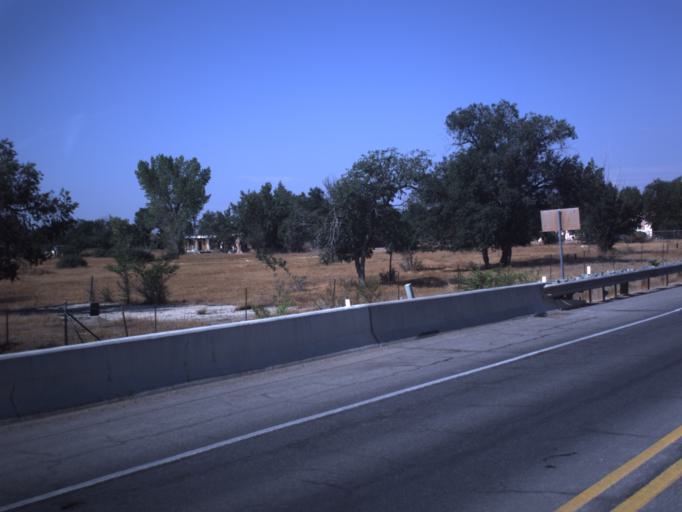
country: US
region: Utah
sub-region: Uintah County
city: Naples
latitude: 40.3697
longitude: -109.3348
